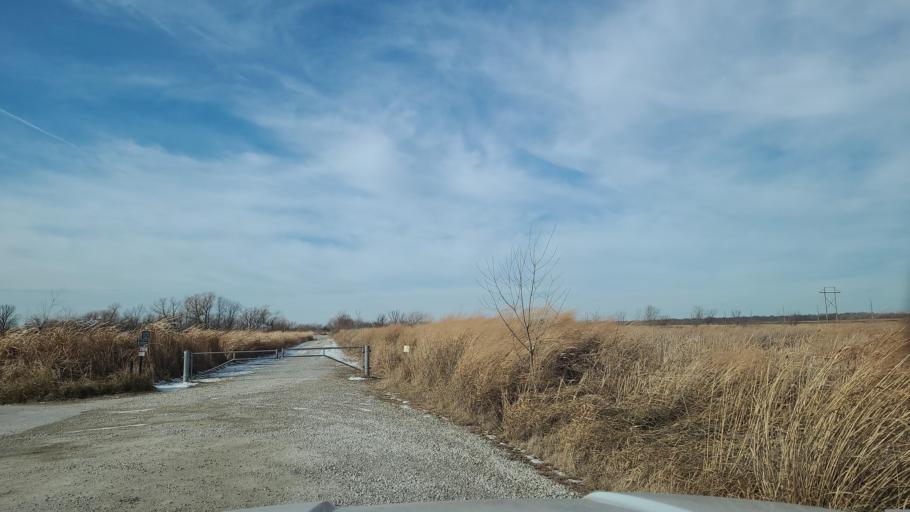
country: US
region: Kansas
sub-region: Douglas County
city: Lawrence
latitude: 38.9209
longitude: -95.2211
